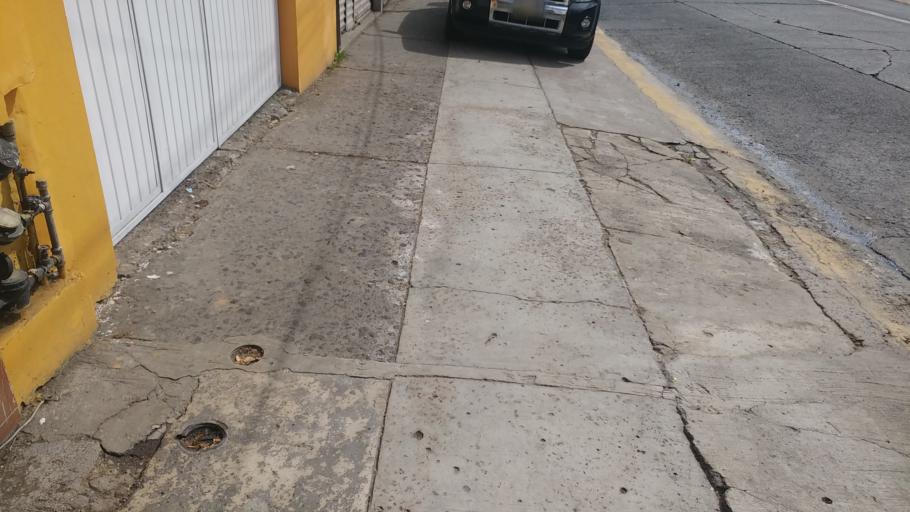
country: MX
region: Veracruz
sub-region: Xalapa
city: Xalapa de Enriquez
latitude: 19.5281
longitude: -96.9116
